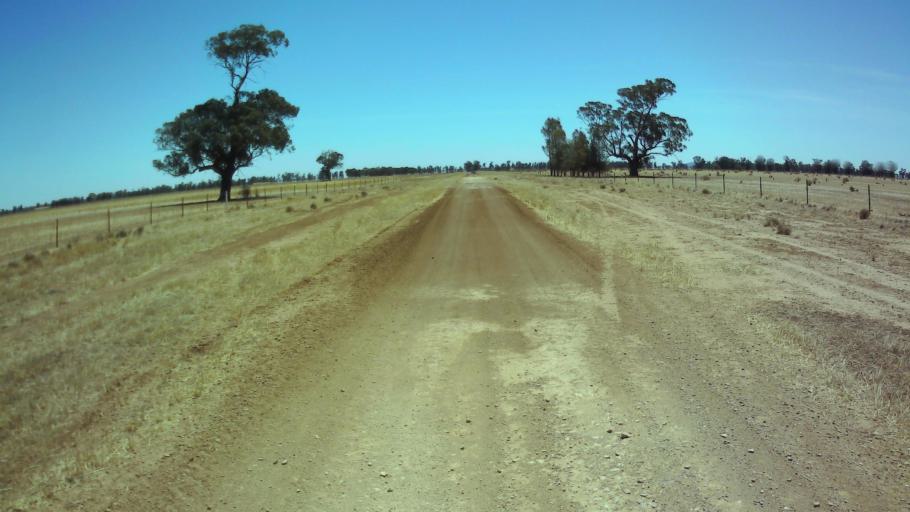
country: AU
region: New South Wales
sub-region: Weddin
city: Grenfell
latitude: -33.9863
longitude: 147.7350
